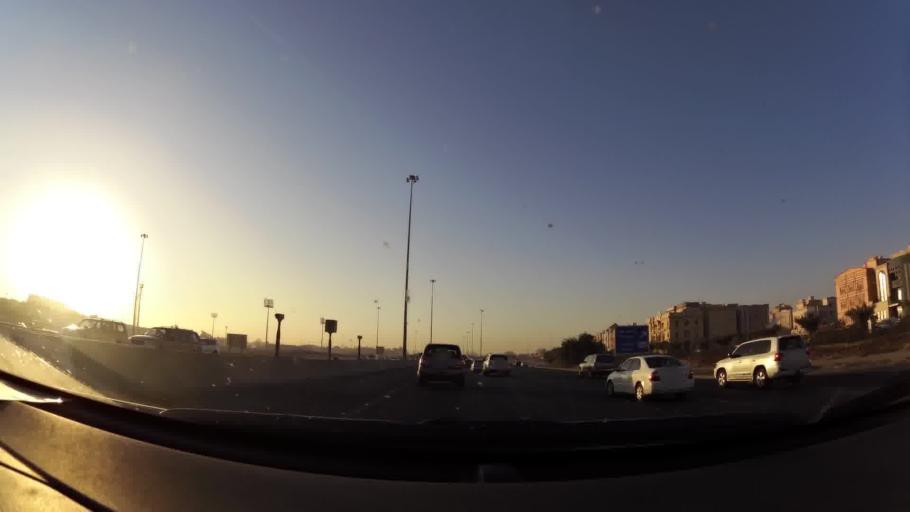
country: KW
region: Al Ahmadi
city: Al Mahbulah
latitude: 29.1248
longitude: 48.1160
